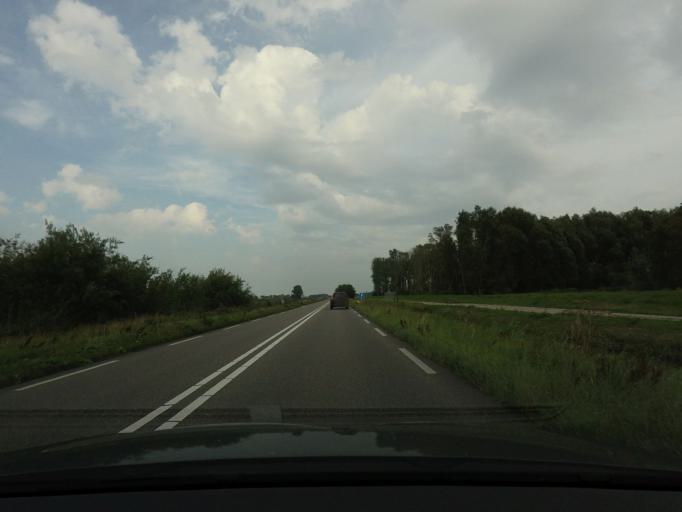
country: NL
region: North Holland
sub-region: Gemeente Schagen
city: Harenkarspel
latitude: 52.6948
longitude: 4.7443
